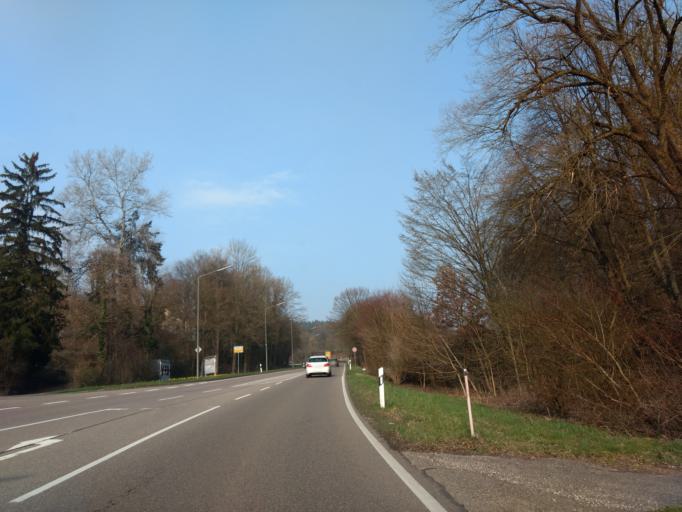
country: DE
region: Baden-Wuerttemberg
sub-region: Regierungsbezirk Stuttgart
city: Lorch
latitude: 48.7990
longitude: 9.6999
